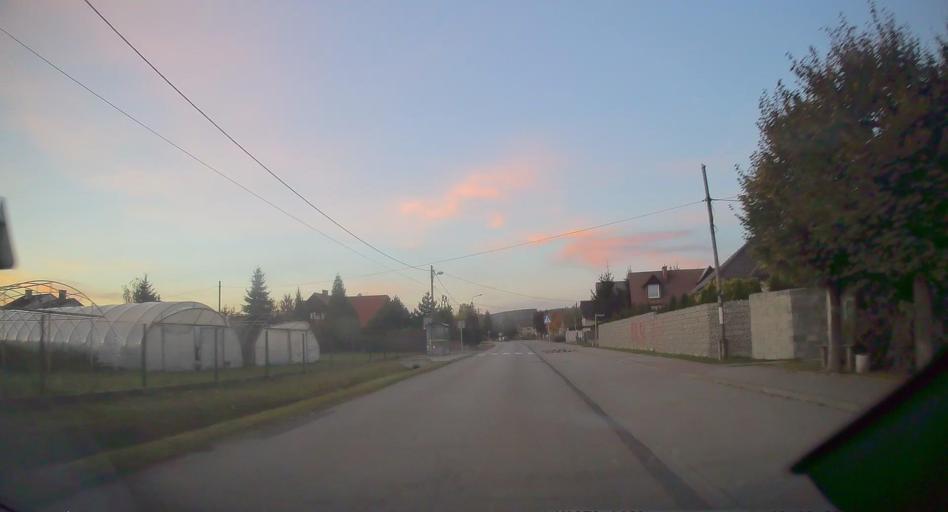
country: PL
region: Lesser Poland Voivodeship
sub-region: Powiat krakowski
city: Zabierzow
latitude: 50.1319
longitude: 19.8217
